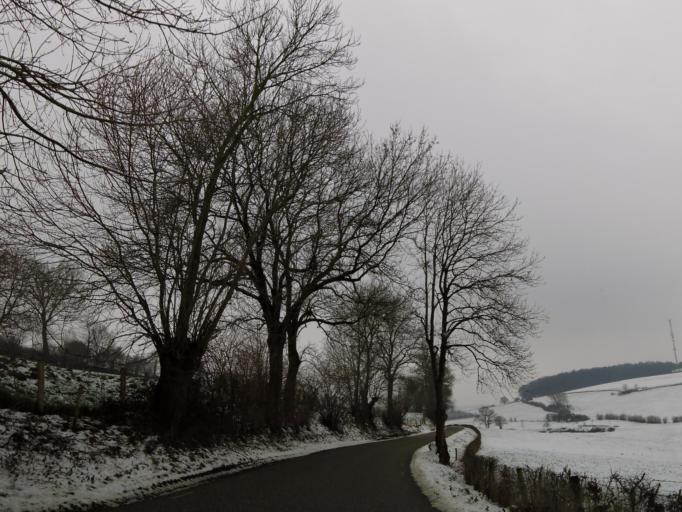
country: NL
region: Limburg
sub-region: Gemeente Voerendaal
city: Ubachsberg
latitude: 50.8327
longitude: 5.9387
